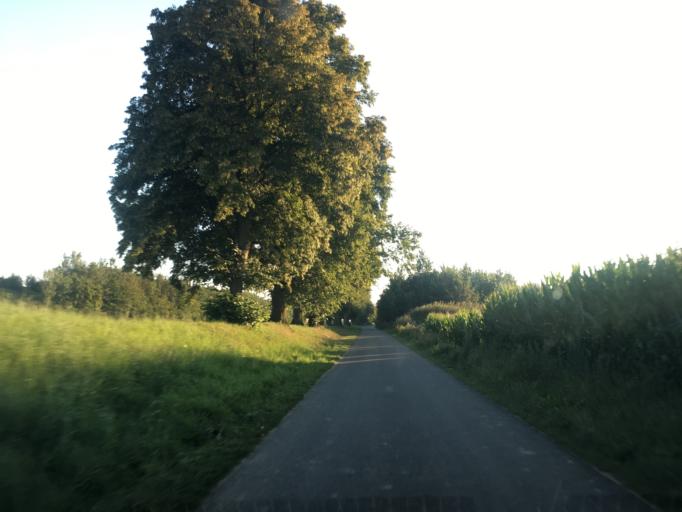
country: DE
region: North Rhine-Westphalia
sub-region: Regierungsbezirk Munster
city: Muenster
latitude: 51.8867
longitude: 7.5914
